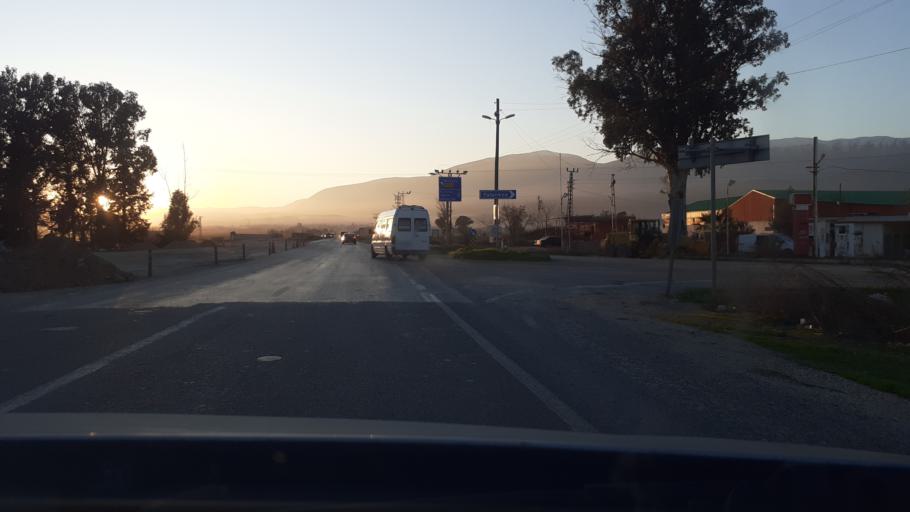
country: TR
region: Hatay
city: Kirikhan
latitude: 36.5052
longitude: 36.4144
